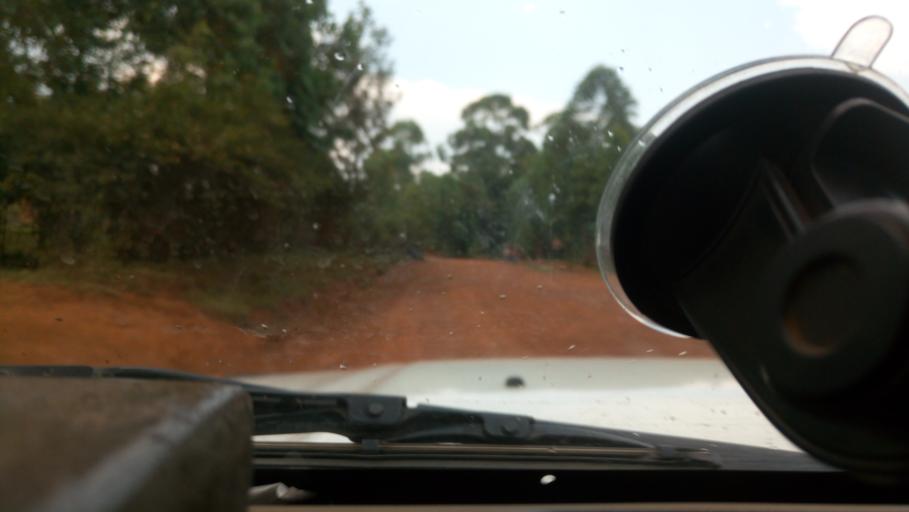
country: KE
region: Kisii
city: Ogembo
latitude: -0.7904
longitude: 34.5826
